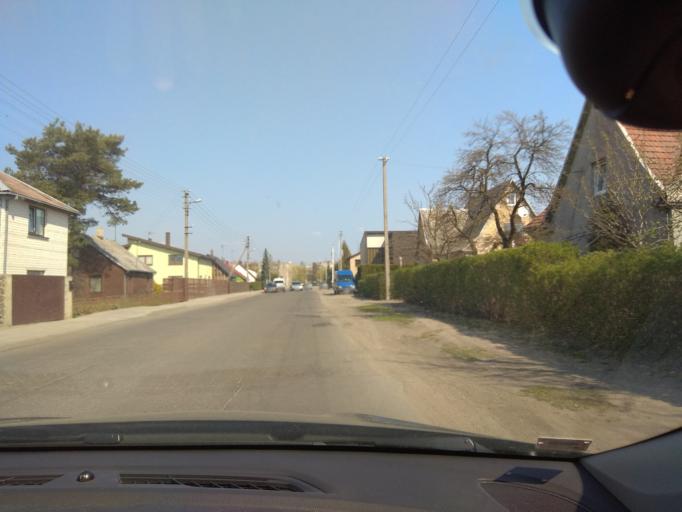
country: LT
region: Marijampoles apskritis
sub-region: Marijampole Municipality
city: Marijampole
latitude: 54.5647
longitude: 23.3500
